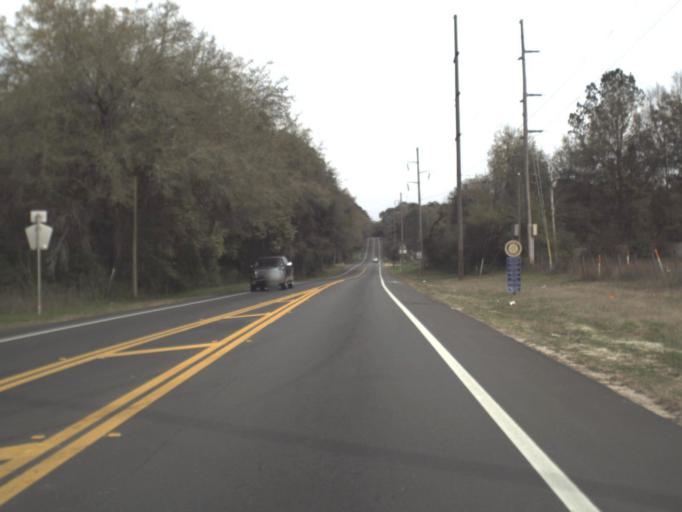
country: US
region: Florida
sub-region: Leon County
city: Tallahassee
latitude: 30.4357
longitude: -84.3728
